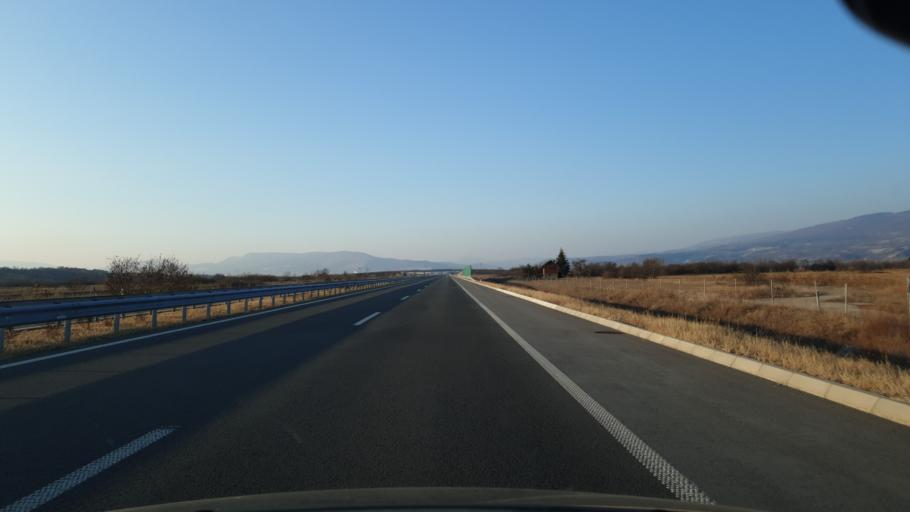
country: RS
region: Central Serbia
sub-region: Pirotski Okrug
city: Pirot
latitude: 43.1001
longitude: 22.6434
